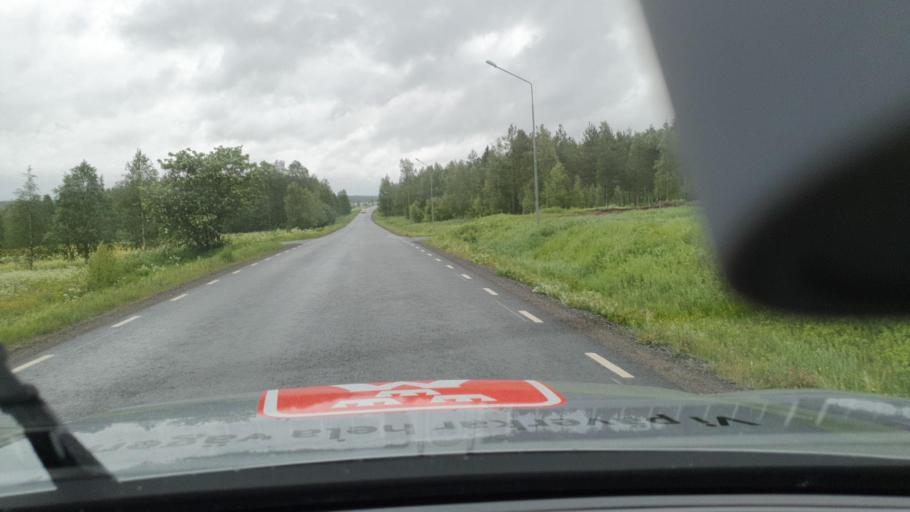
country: FI
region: Lapland
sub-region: Torniolaakso
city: Ylitornio
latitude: 66.1861
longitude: 23.7557
